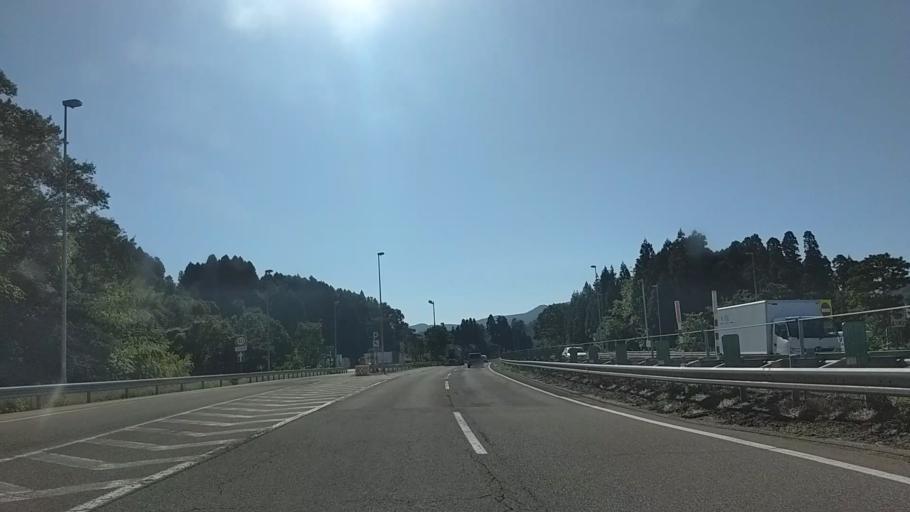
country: JP
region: Ishikawa
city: Tsubata
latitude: 36.6055
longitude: 136.7199
